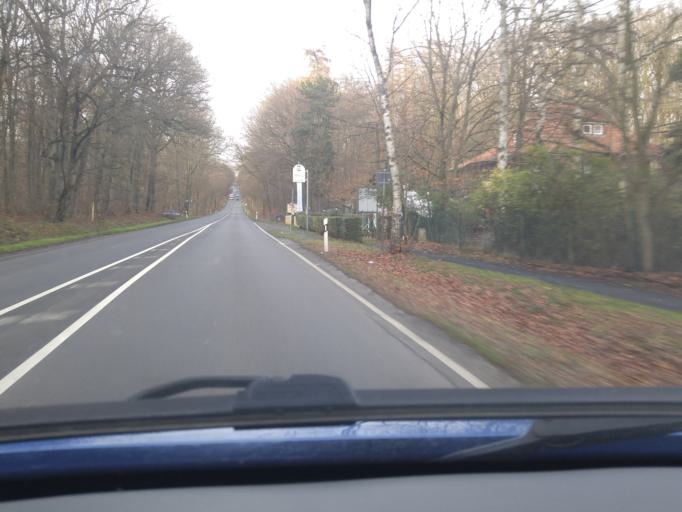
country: DE
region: Hesse
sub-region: Regierungsbezirk Darmstadt
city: Konigstein im Taunus
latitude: 50.1655
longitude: 8.4811
